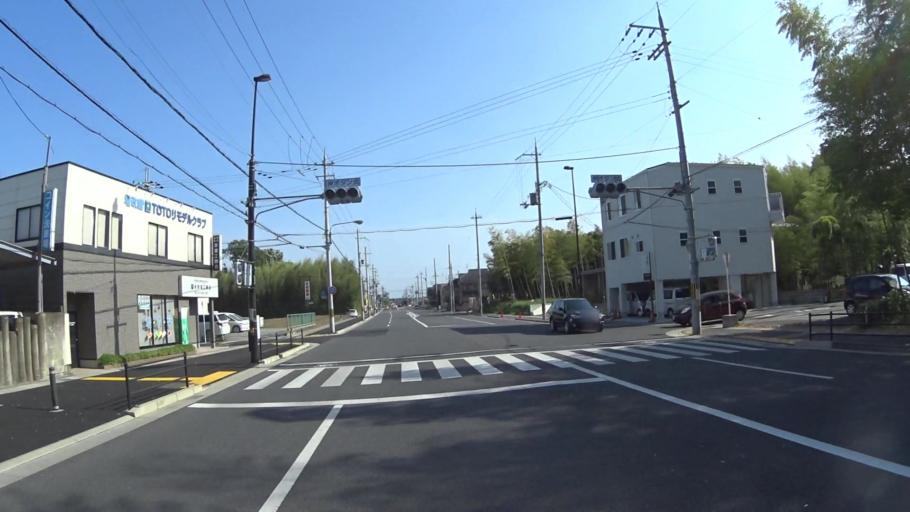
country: JP
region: Kyoto
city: Muko
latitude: 34.9421
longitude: 135.6858
